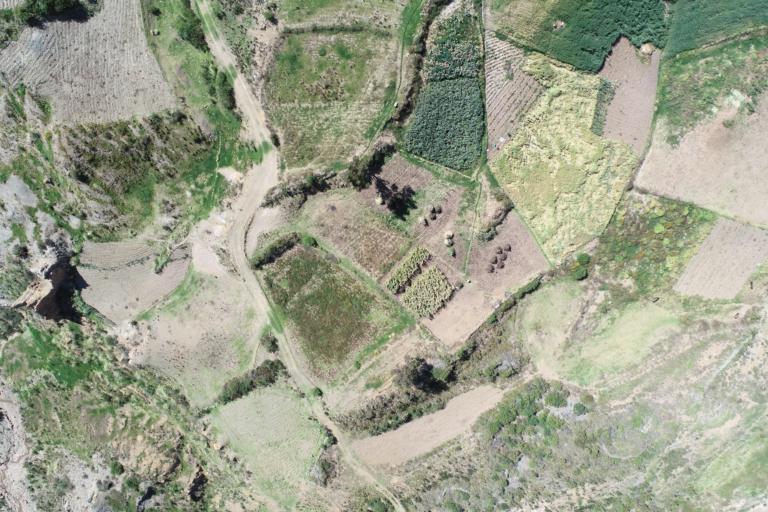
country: BO
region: La Paz
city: La Paz
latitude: -16.5558
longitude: -67.9896
